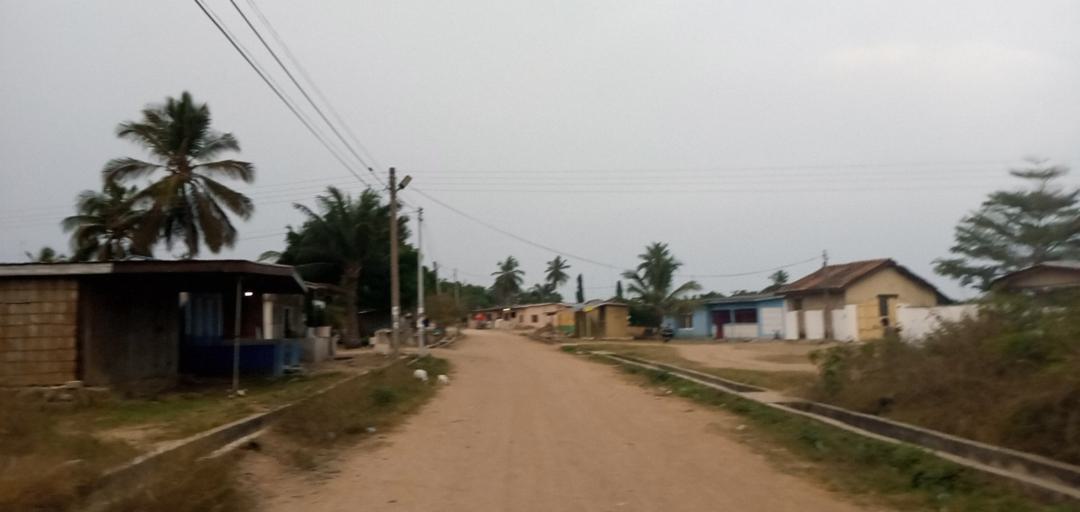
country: GH
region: Central
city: Winneba
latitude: 5.3553
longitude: -0.6285
